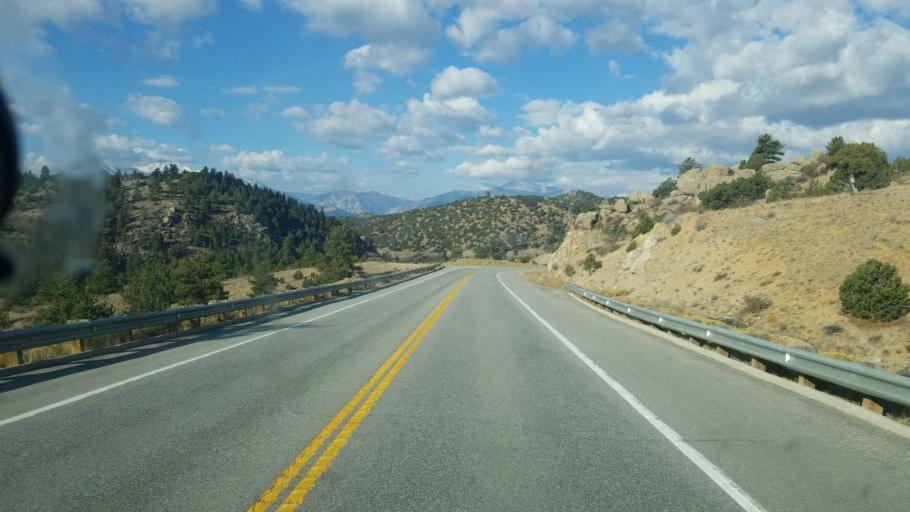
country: US
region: Colorado
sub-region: Chaffee County
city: Buena Vista
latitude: 38.8409
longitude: -106.0026
